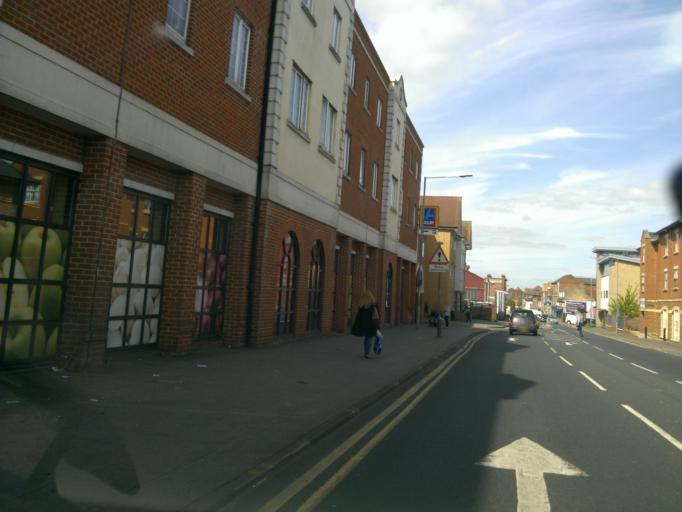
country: GB
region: England
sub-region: Essex
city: Colchester
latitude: 51.8854
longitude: 0.9095
